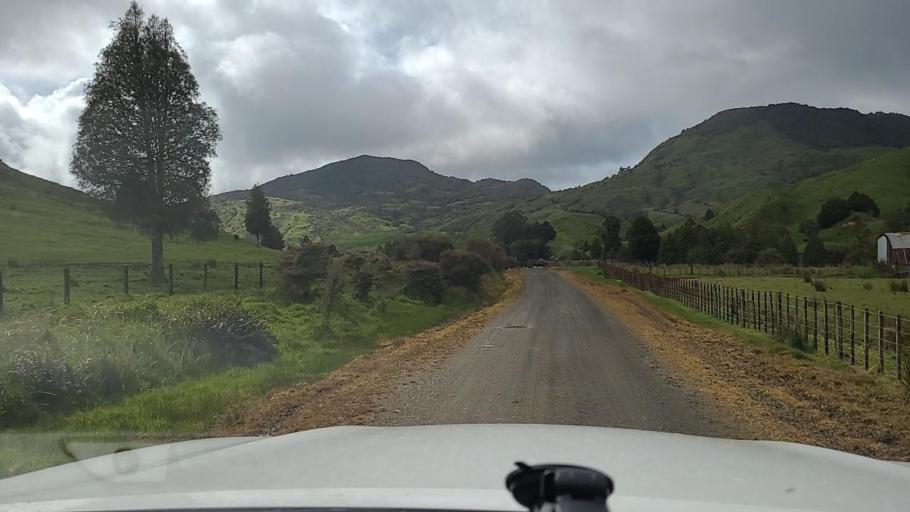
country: NZ
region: Bay of Plenty
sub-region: Opotiki District
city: Opotiki
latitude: -38.3169
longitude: 177.5751
